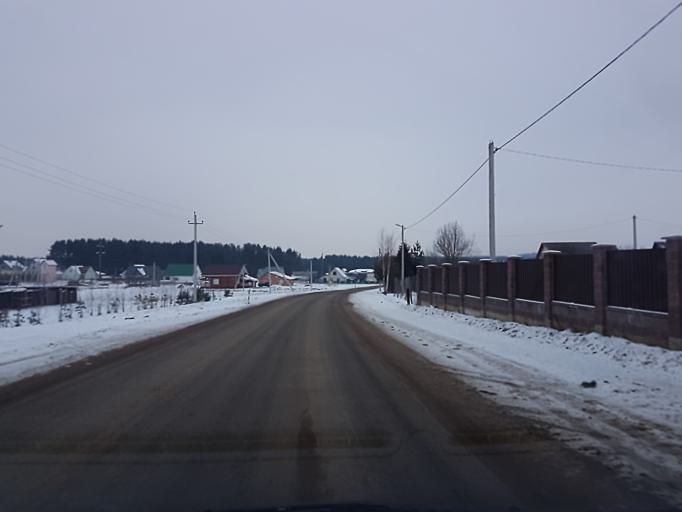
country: BY
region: Minsk
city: Rakaw
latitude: 53.9627
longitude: 27.0410
